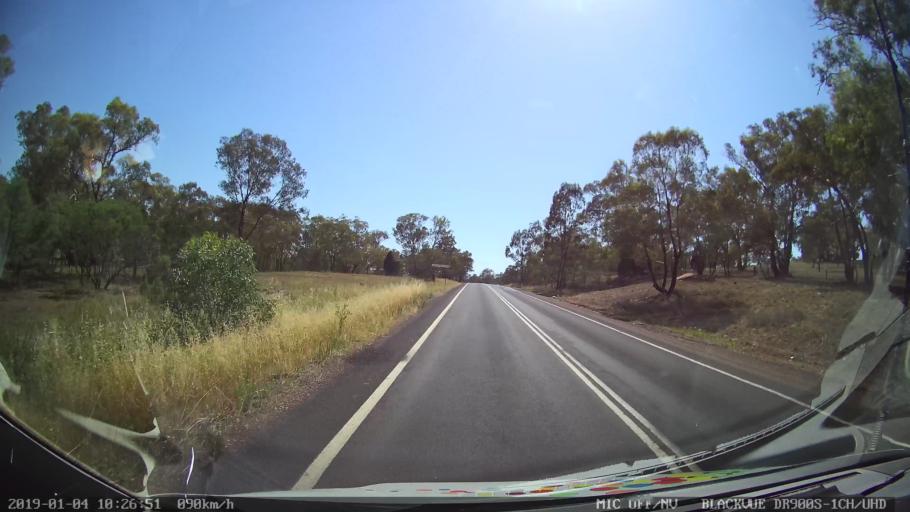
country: AU
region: New South Wales
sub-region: Cabonne
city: Canowindra
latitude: -33.3747
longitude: 148.5914
